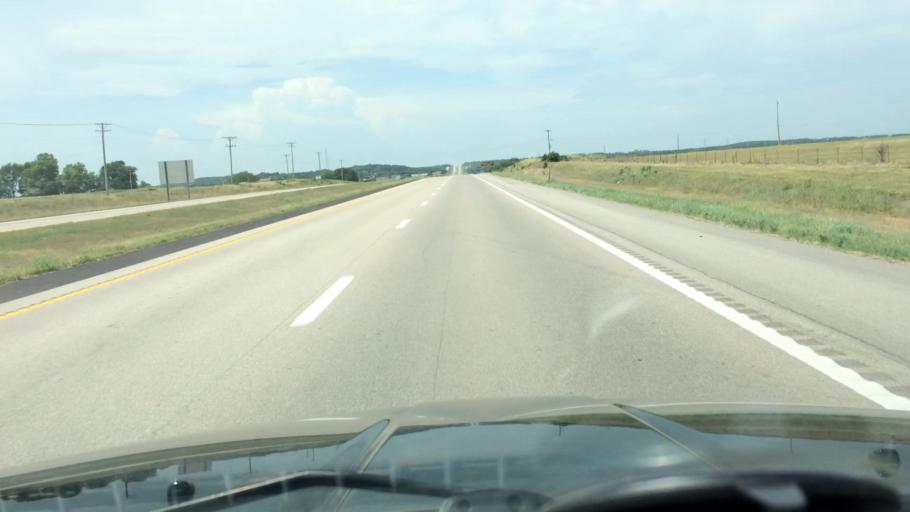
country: US
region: Missouri
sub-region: Polk County
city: Bolivar
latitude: 37.6034
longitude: -93.4402
